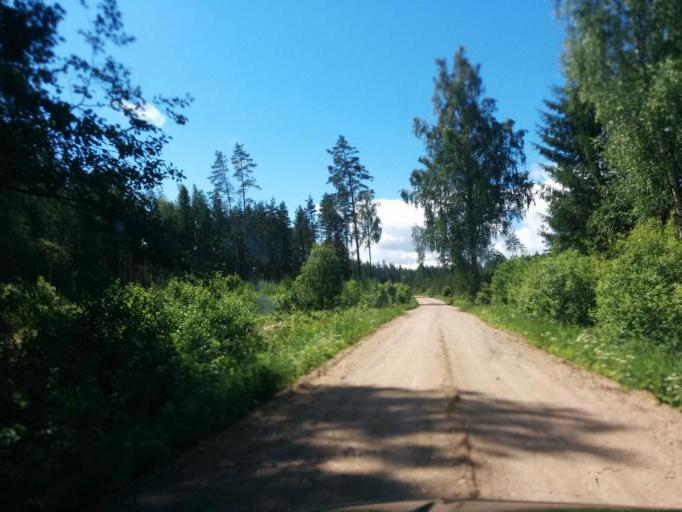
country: LV
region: Vilaka
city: Vilaka
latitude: 57.3217
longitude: 27.6679
